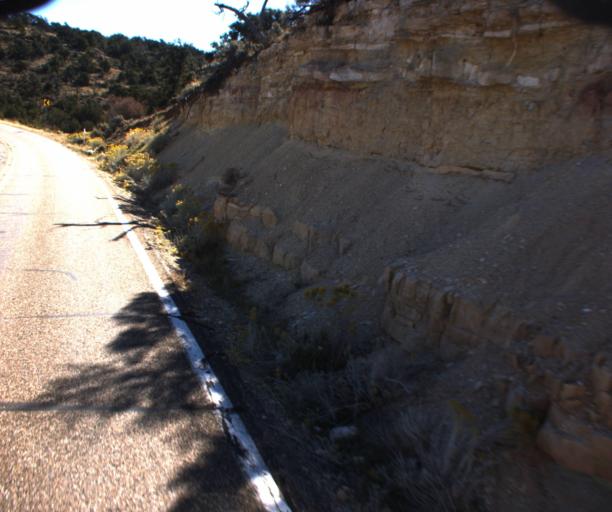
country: US
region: Arizona
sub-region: Coconino County
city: Fredonia
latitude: 36.8467
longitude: -112.2622
